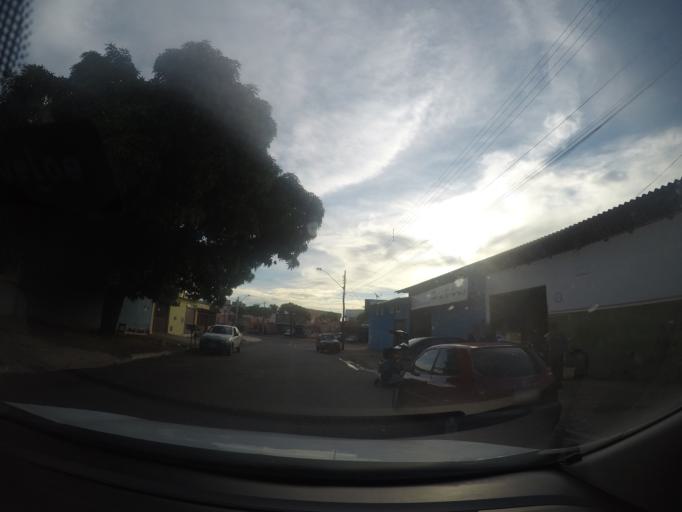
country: BR
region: Goias
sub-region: Goiania
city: Goiania
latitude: -16.6845
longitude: -49.3200
